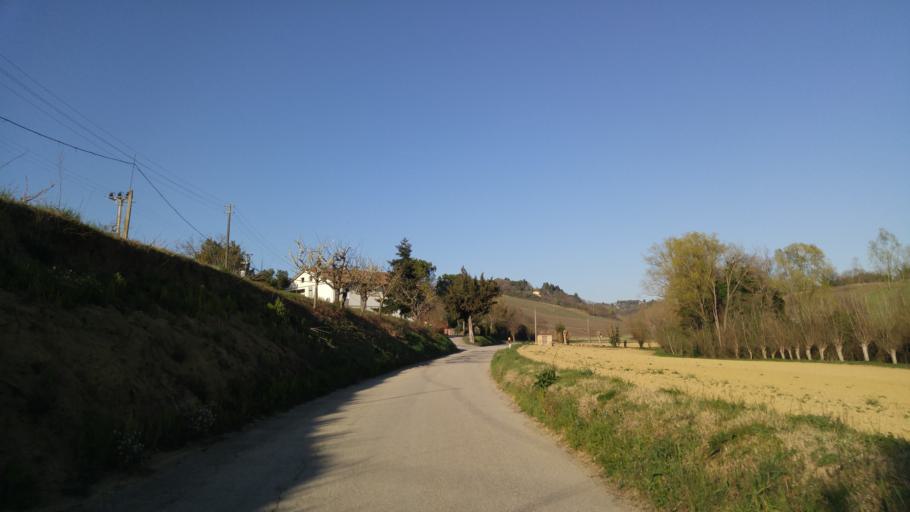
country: IT
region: The Marches
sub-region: Provincia di Pesaro e Urbino
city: Fenile
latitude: 43.8432
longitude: 12.9157
